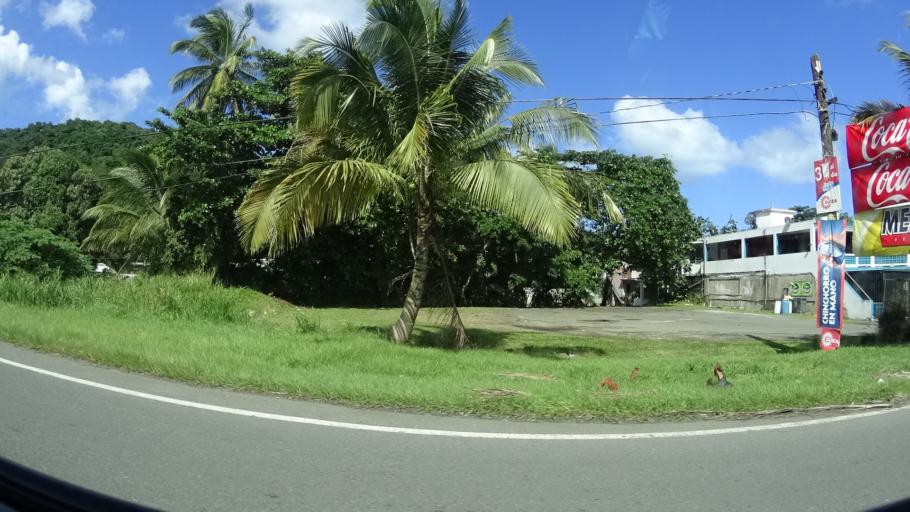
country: PR
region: Rio Grande
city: Palmer
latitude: 18.3722
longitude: -65.7680
